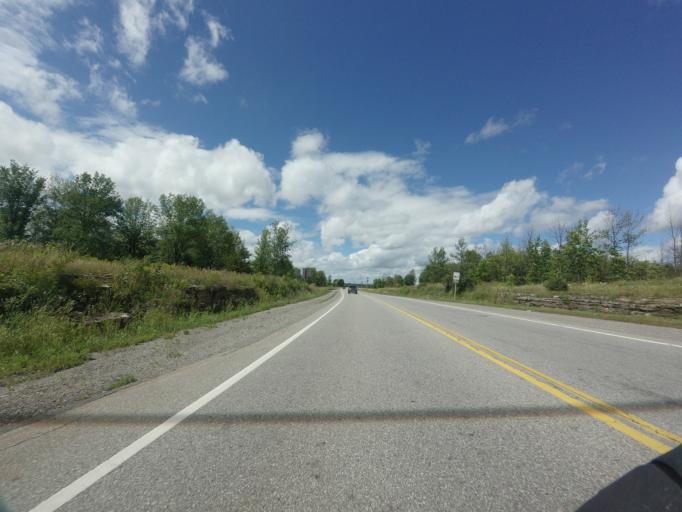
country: CA
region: Ontario
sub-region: Lanark County
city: Smiths Falls
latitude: 44.9180
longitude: -76.0242
